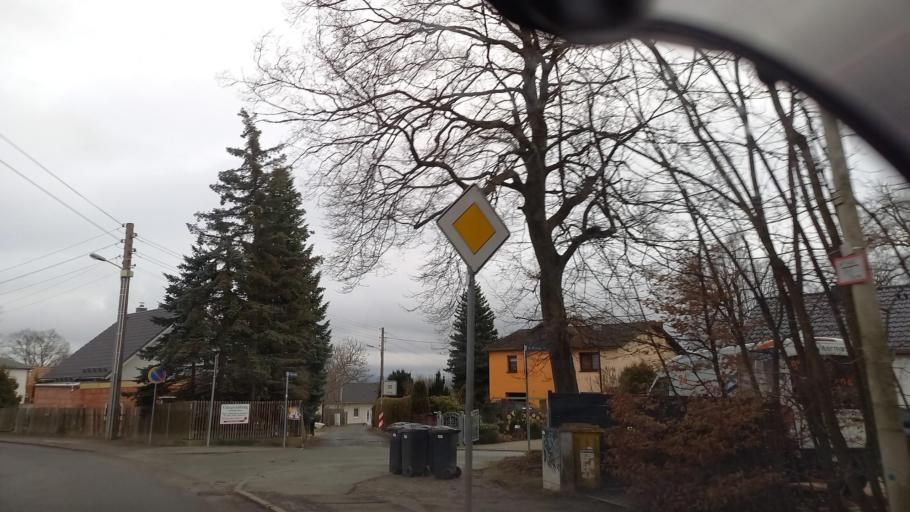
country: DE
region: Saxony
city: Wilkau-Hasslau
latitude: 50.6721
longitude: 12.4828
